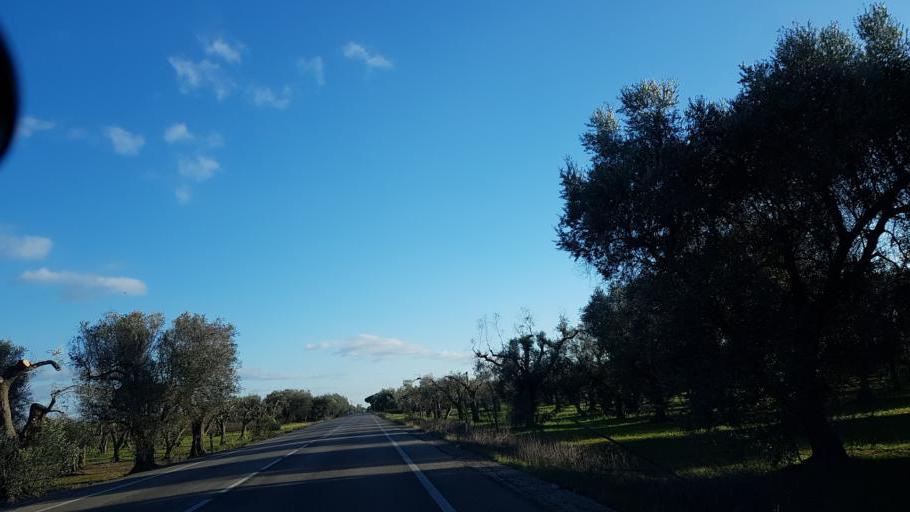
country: IT
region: Apulia
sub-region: Provincia di Lecce
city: Squinzano
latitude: 40.4567
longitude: 18.0237
